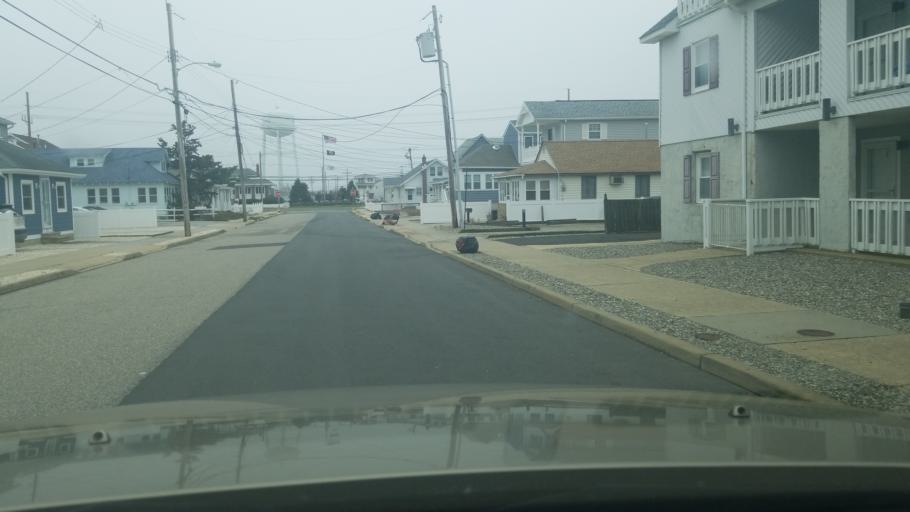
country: US
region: New Jersey
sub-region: Ocean County
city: Seaside Park
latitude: 39.9351
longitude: -74.0749
